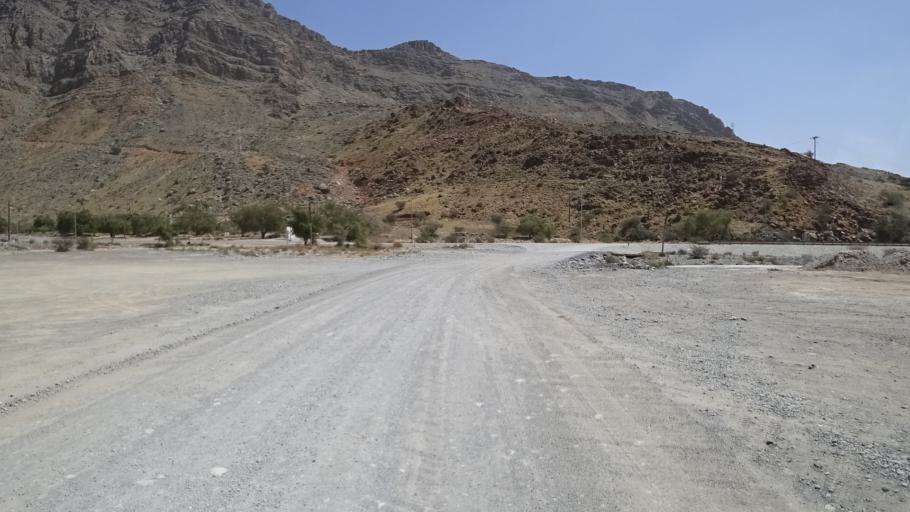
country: OM
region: Muhafazat ad Dakhiliyah
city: Izki
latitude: 22.9498
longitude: 57.6709
